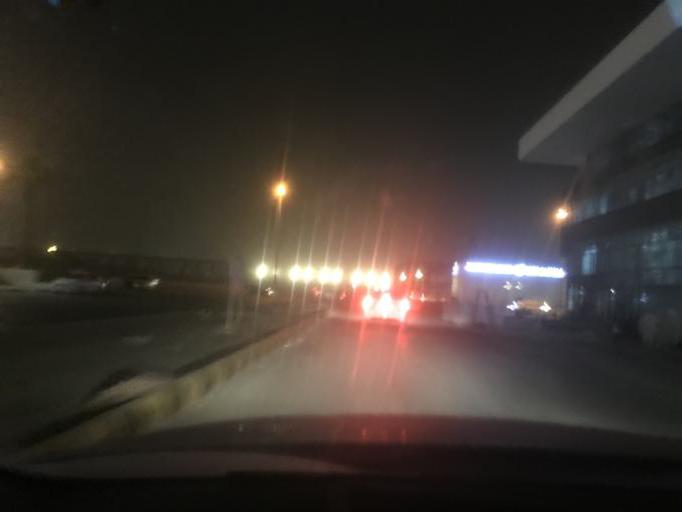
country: SA
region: Ar Riyad
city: Riyadh
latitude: 24.8323
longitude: 46.7334
